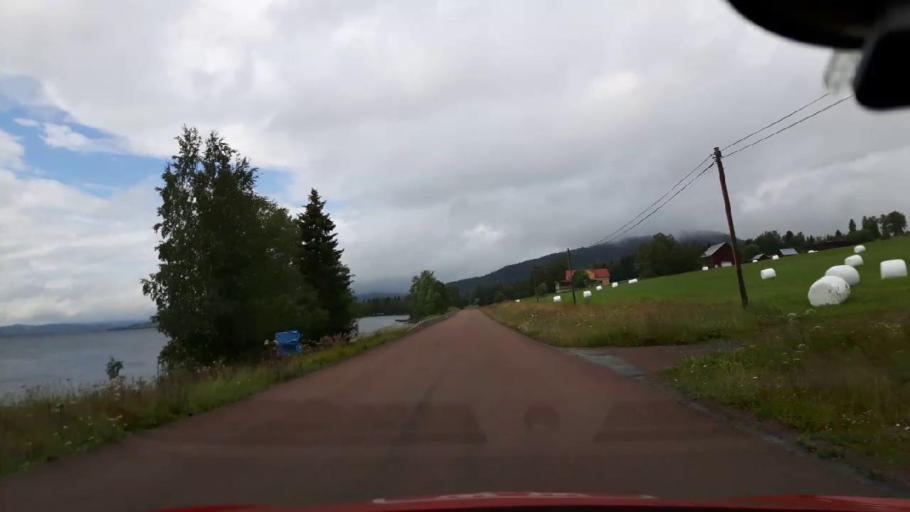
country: SE
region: Jaemtland
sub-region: Krokoms Kommun
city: Valla
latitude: 63.3714
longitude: 14.0333
